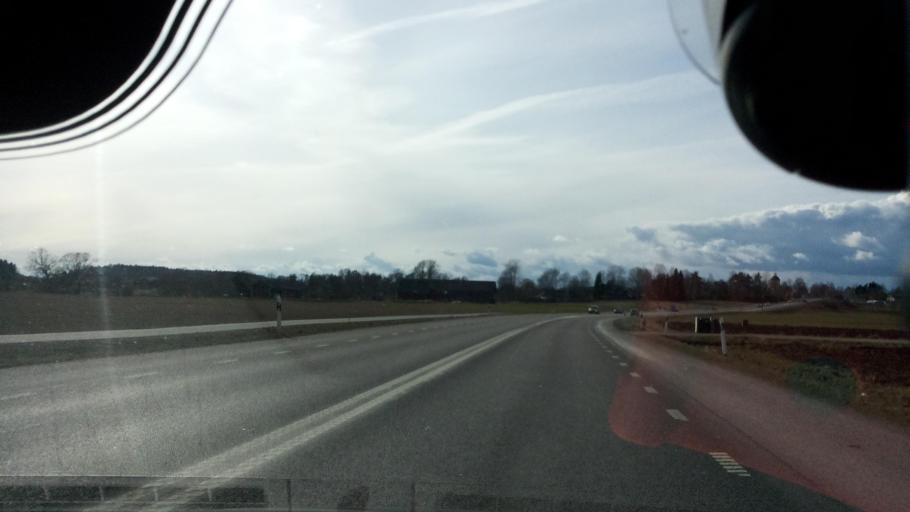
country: SE
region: Soedermanland
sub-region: Trosa Kommun
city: Vagnharad
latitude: 58.9460
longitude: 17.5155
